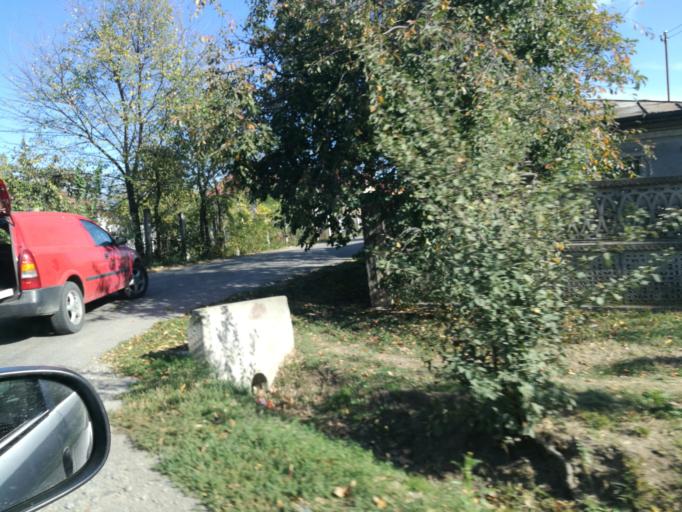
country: RO
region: Giurgiu
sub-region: Comuna Joita
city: Bacu
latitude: 44.4753
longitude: 25.8899
